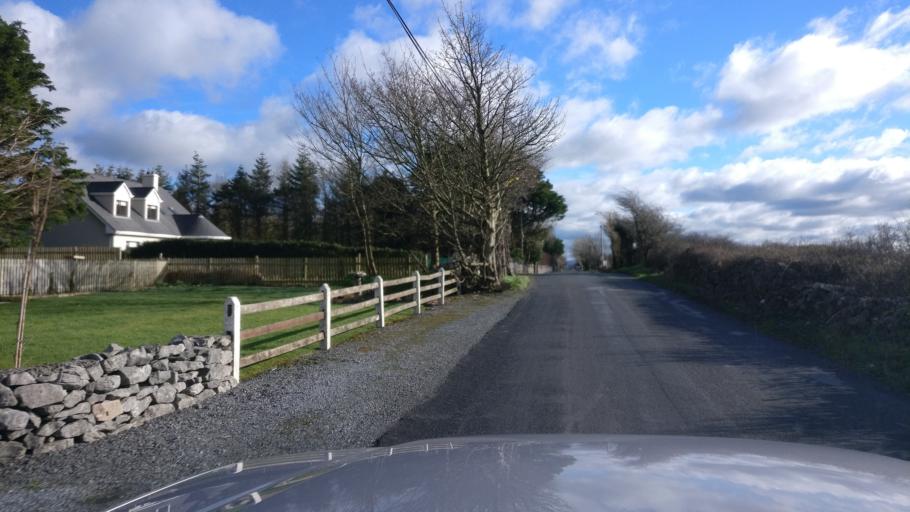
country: IE
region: Connaught
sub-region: County Galway
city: Oranmore
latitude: 53.2624
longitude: -8.8652
